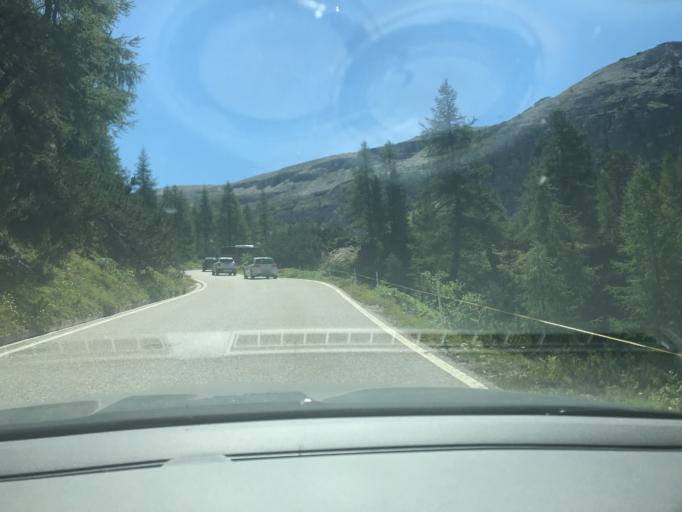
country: IT
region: Trentino-Alto Adige
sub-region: Bolzano
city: Sesto
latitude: 46.6078
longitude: 12.2883
